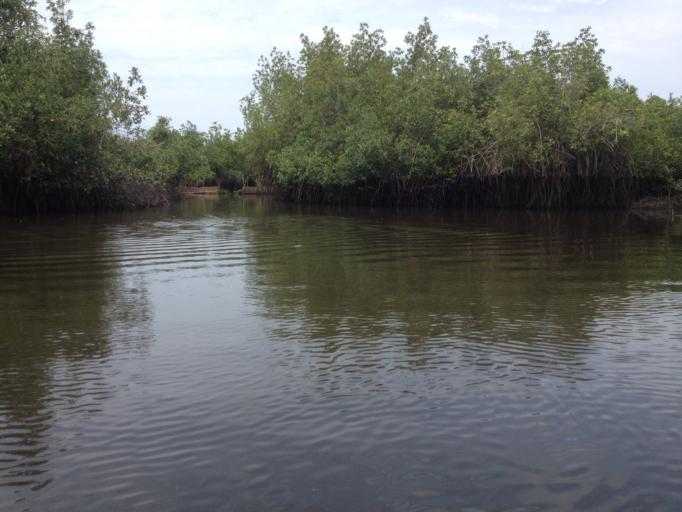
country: BJ
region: Mono
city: Grand-Popo
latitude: 6.3142
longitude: 1.9128
